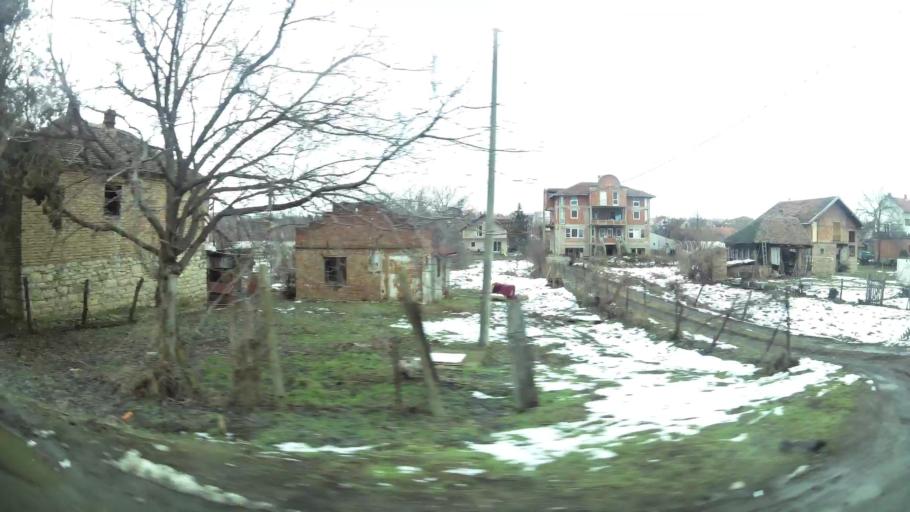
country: RS
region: Central Serbia
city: Sremcica
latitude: 44.7217
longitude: 20.3708
